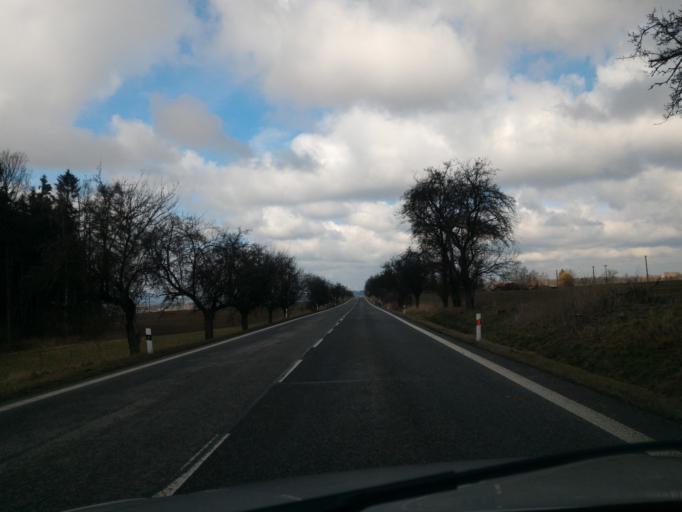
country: PL
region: Silesian Voivodeship
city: Zawidow
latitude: 51.0065
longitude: 15.0703
